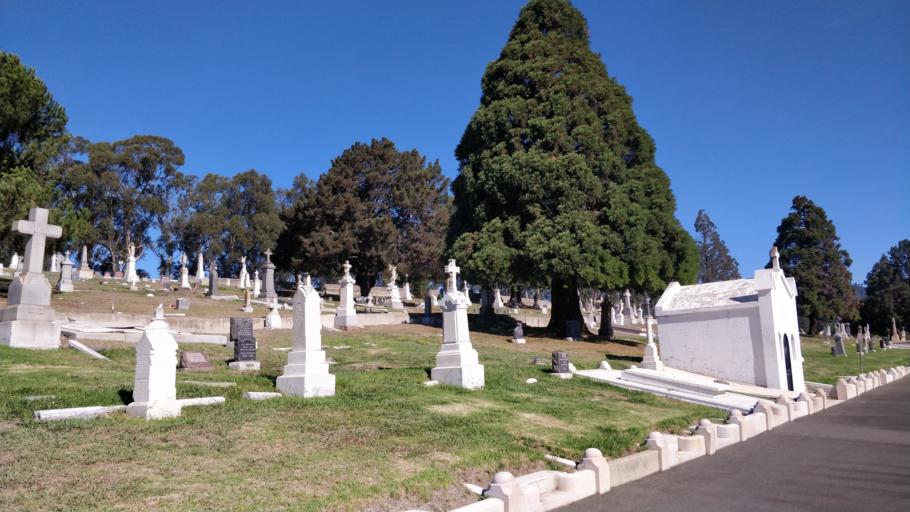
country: US
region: California
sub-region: Alameda County
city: Piedmont
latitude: 37.8332
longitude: -122.2452
